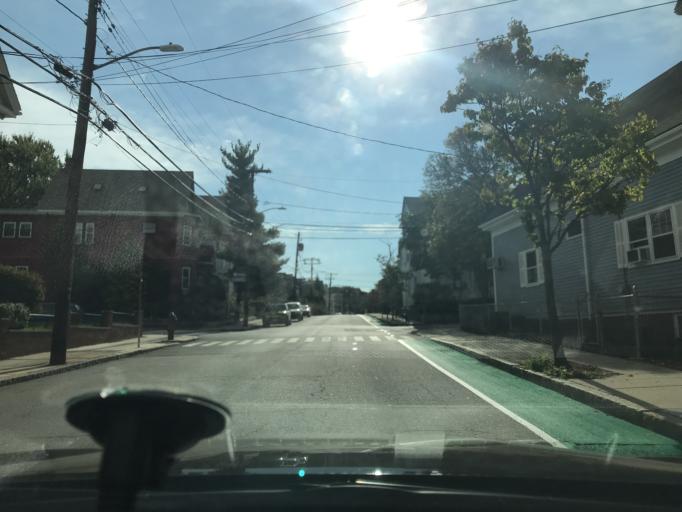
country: US
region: Massachusetts
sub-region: Middlesex County
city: Somerville
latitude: 42.3922
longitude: -71.1163
